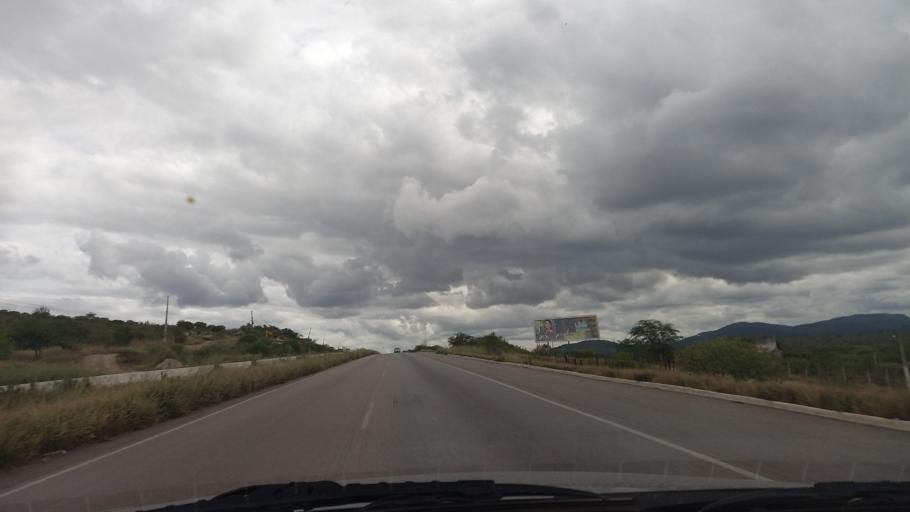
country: BR
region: Pernambuco
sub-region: Caruaru
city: Caruaru
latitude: -8.3223
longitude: -36.0934
